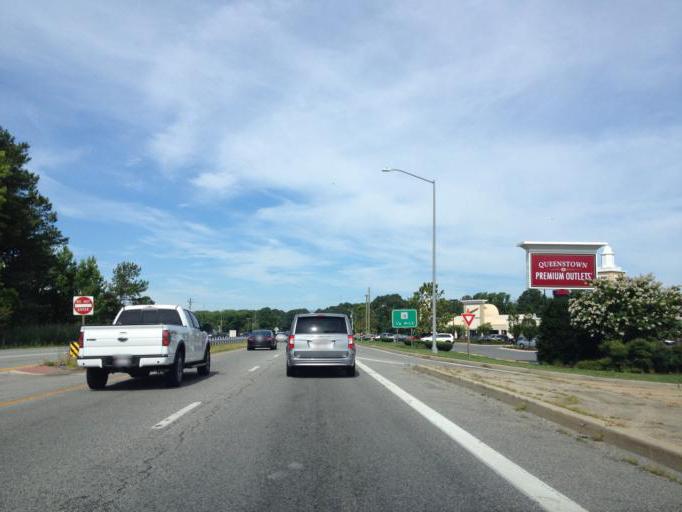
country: US
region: Maryland
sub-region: Queen Anne's County
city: Grasonville
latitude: 38.9819
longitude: -76.1589
